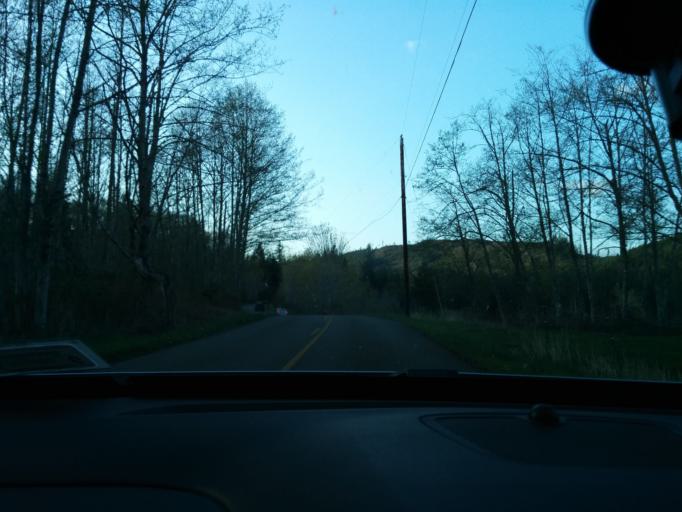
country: US
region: Washington
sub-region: Snohomish County
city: Gold Bar
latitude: 47.8822
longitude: -121.7344
